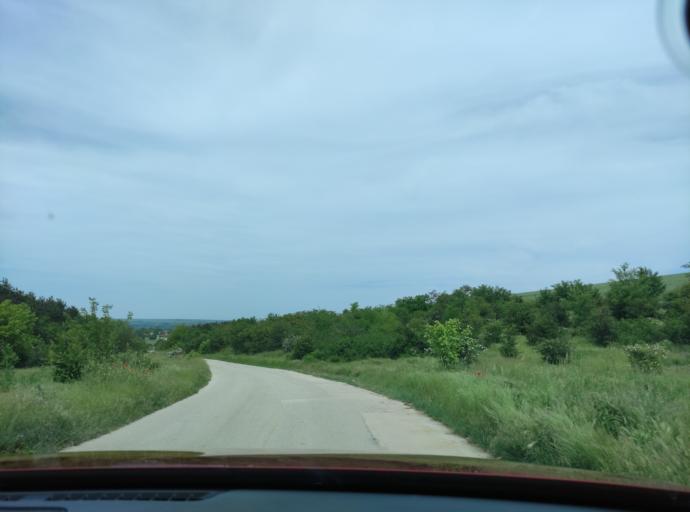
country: BG
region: Pleven
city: Iskur
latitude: 43.5335
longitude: 24.3009
